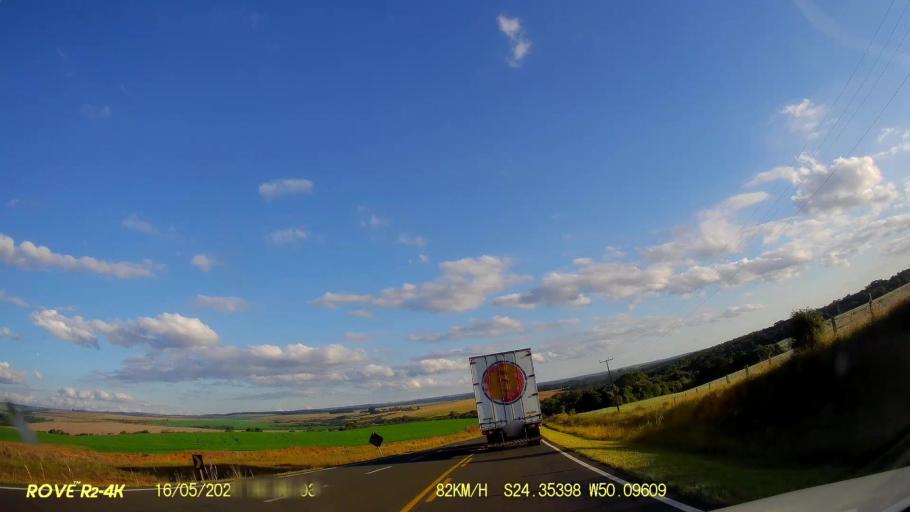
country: BR
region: Parana
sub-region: Pirai Do Sul
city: Pirai do Sul
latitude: -24.3541
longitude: -50.0958
